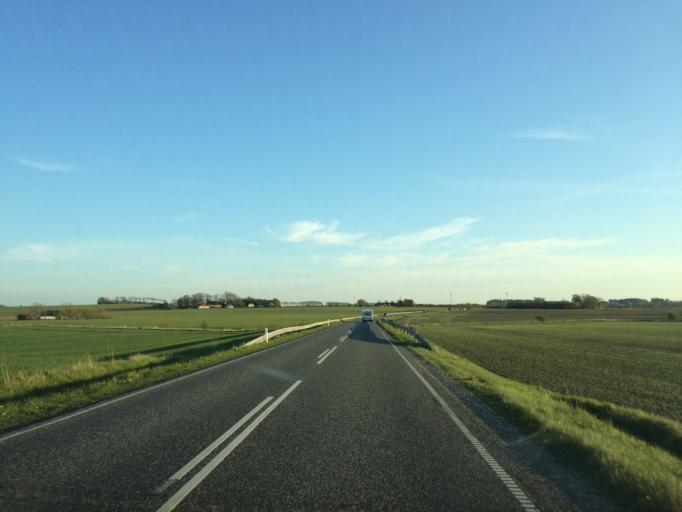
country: DK
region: Central Jutland
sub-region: Struer Kommune
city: Struer
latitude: 56.4446
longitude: 8.5333
